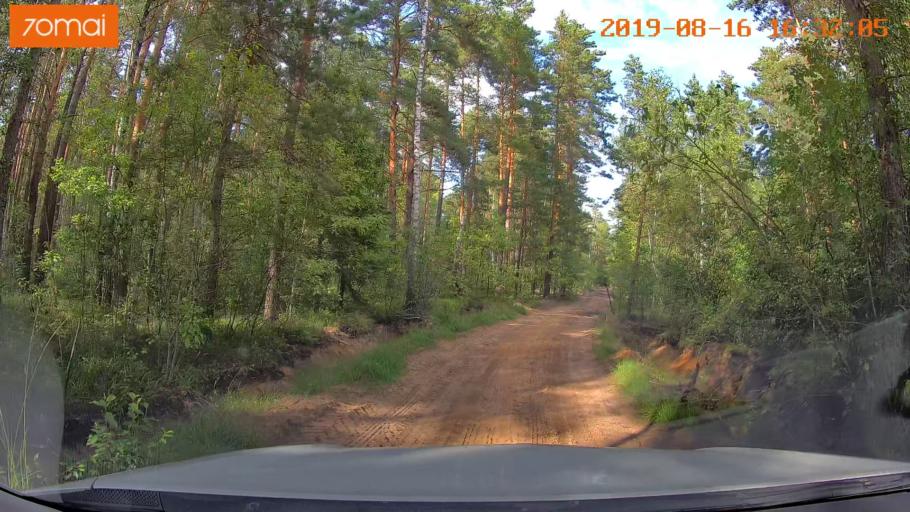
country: BY
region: Mogilev
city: Asipovichy
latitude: 53.2271
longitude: 28.7734
